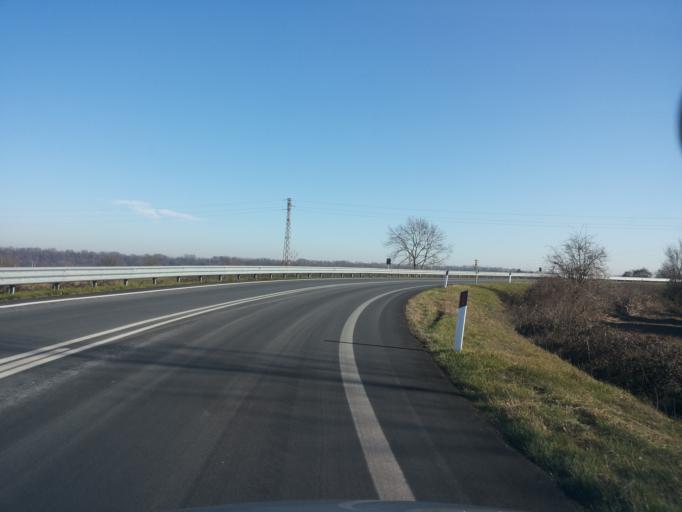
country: IT
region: Piedmont
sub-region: Provincia di Biella
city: Benna
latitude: 45.5046
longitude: 8.1279
